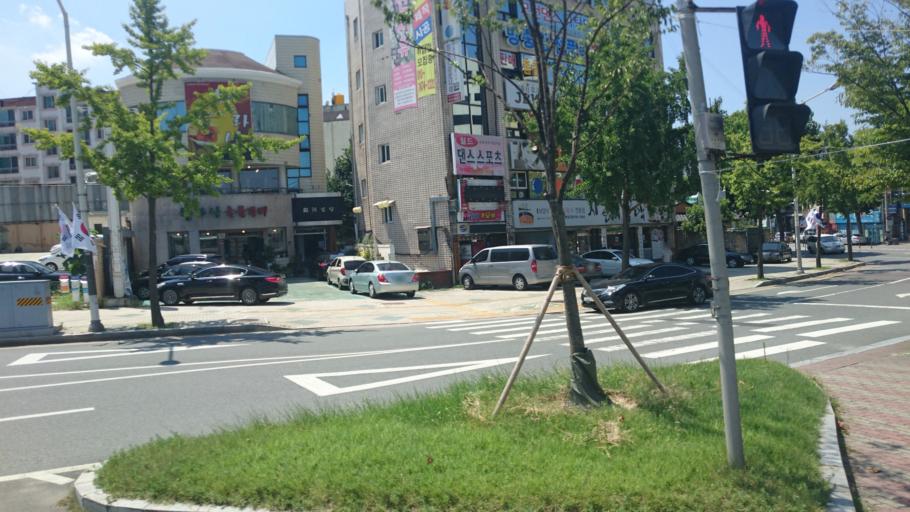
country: KR
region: Daegu
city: Daegu
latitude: 35.8833
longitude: 128.6240
